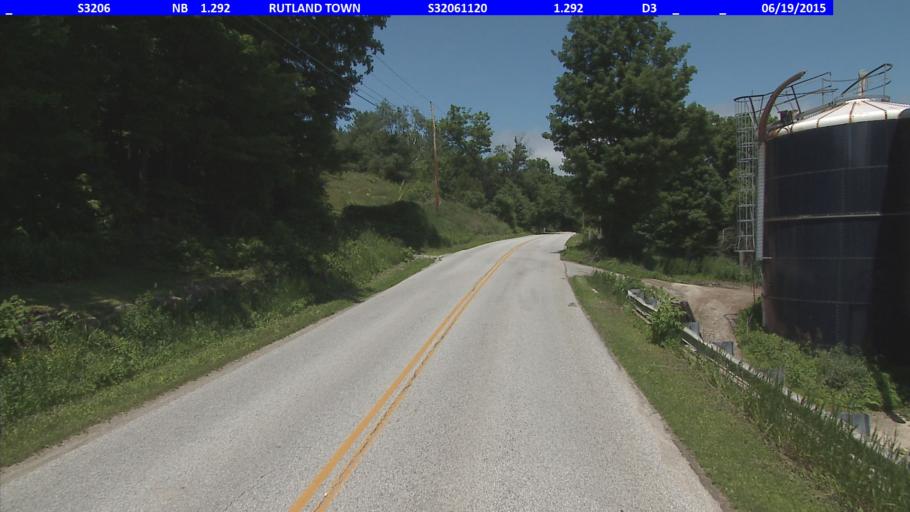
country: US
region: Vermont
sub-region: Rutland County
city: Rutland
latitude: 43.6473
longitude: -72.9958
